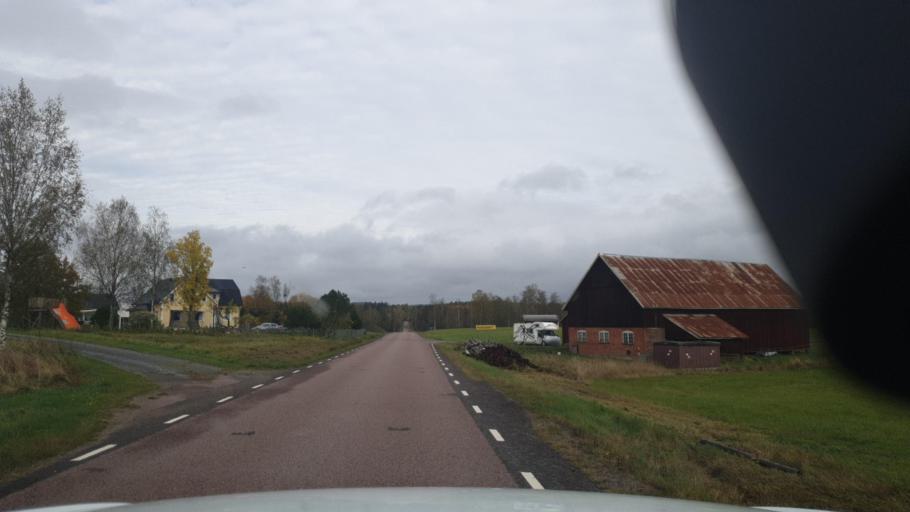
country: SE
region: Vaermland
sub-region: Karlstads Kommun
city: Edsvalla
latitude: 59.4872
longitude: 13.0919
